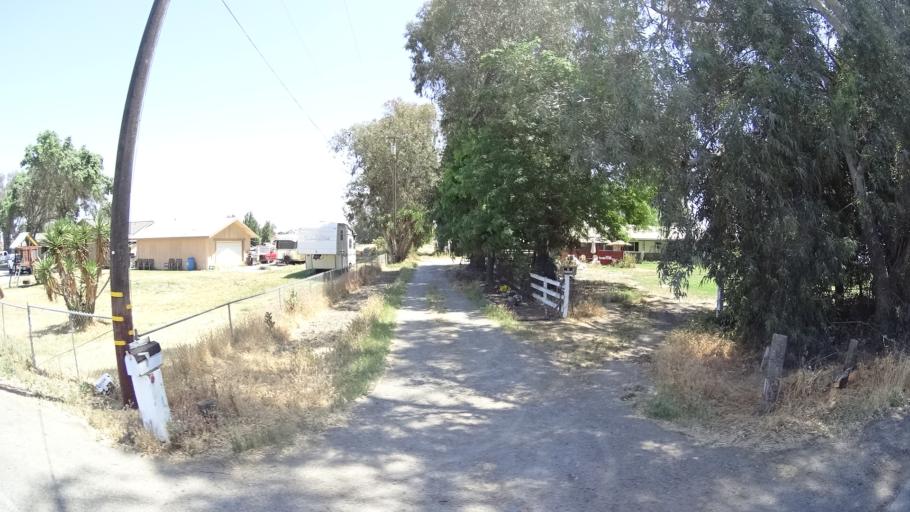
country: US
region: California
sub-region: Kings County
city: Lemoore
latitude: 36.2736
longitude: -119.7629
